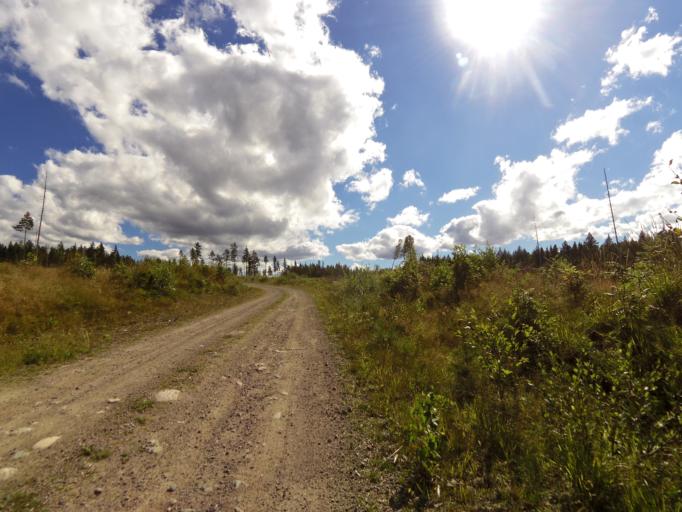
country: SE
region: Gaevleborg
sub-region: Hofors Kommun
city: Hofors
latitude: 60.5268
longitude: 16.2328
